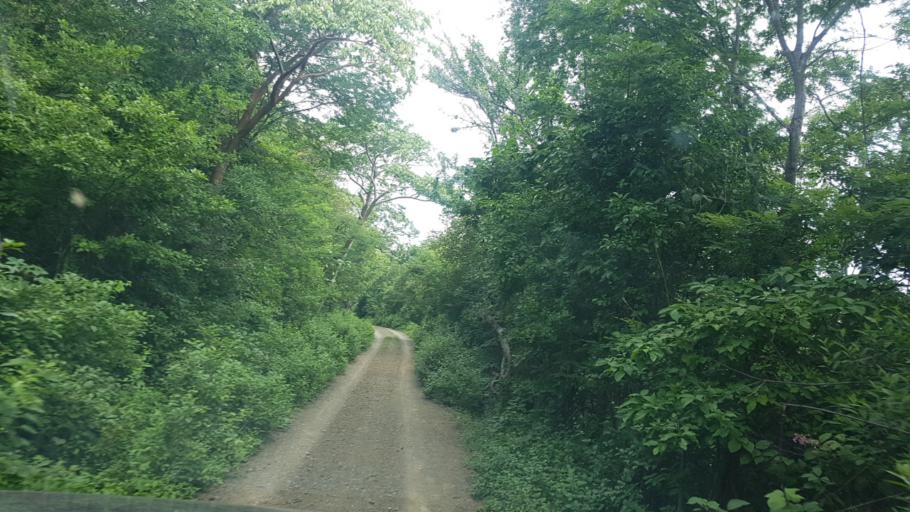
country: NI
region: Nueva Segovia
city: Ciudad Antigua
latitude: 13.5964
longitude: -86.3684
